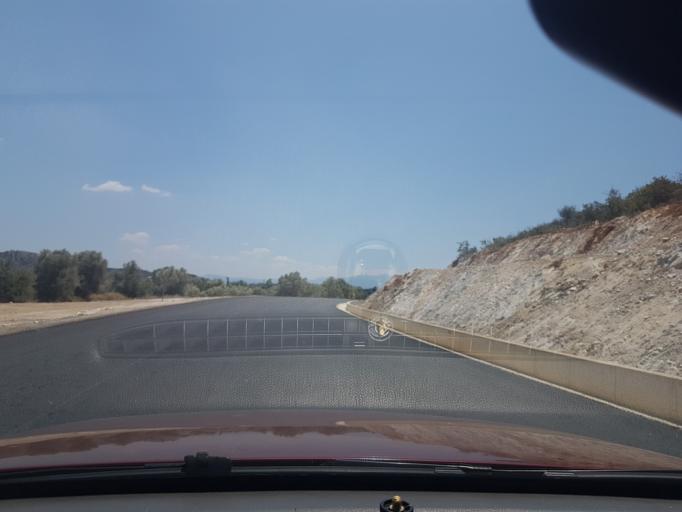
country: GR
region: Central Greece
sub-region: Nomos Evvoias
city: Filla
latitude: 38.4467
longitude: 23.6729
